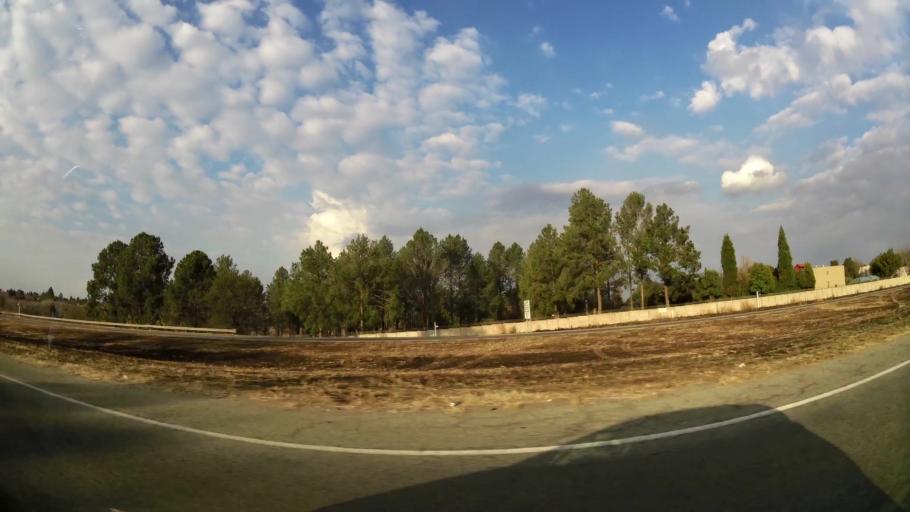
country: ZA
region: Gauteng
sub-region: Sedibeng District Municipality
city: Vanderbijlpark
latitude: -26.7525
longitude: 27.8258
